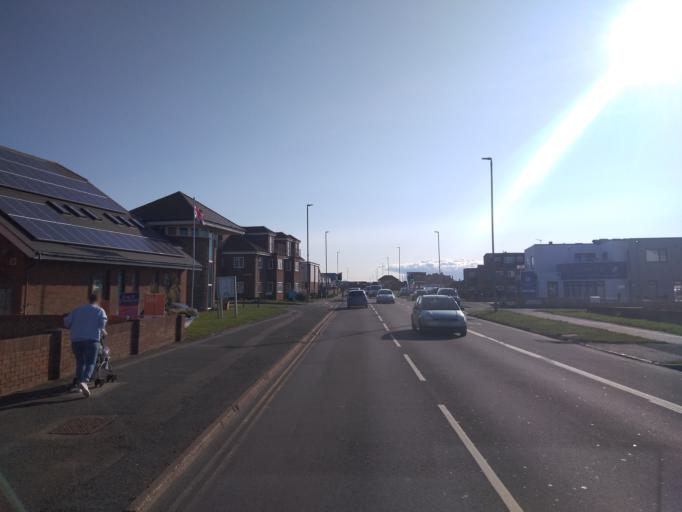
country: GB
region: England
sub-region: East Sussex
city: Peacehaven
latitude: 50.7942
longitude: -0.0150
